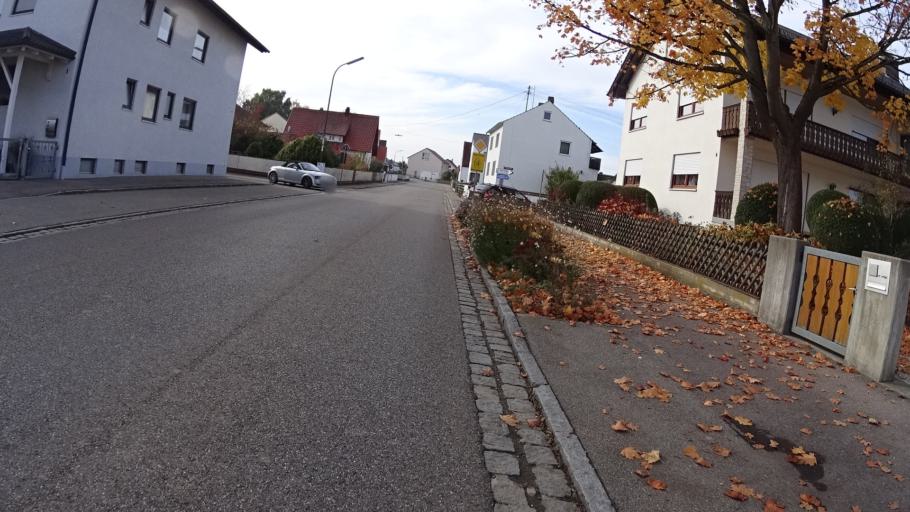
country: DE
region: Bavaria
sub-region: Upper Bavaria
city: Eitensheim
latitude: 48.8187
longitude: 11.3177
